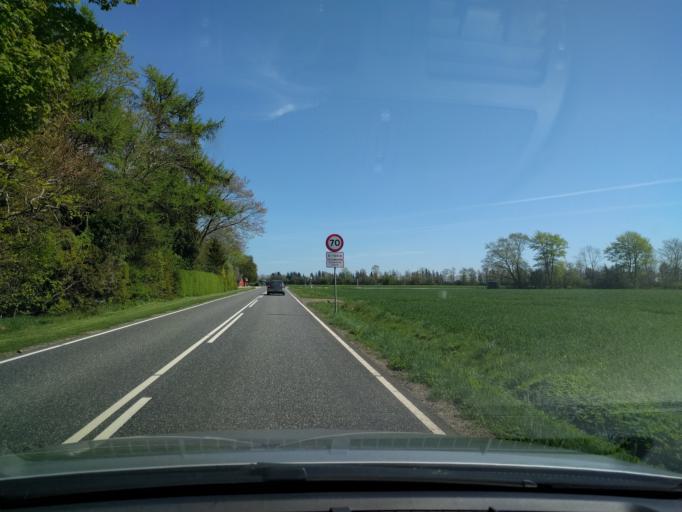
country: DK
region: South Denmark
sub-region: Billund Kommune
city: Grindsted
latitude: 55.6789
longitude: 9.0020
